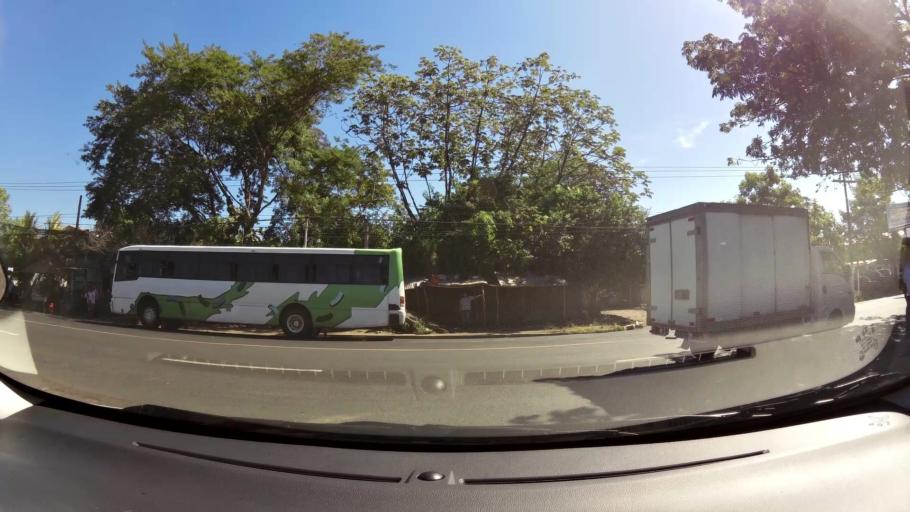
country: SV
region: San Miguel
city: San Miguel
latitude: 13.4954
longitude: -88.1720
